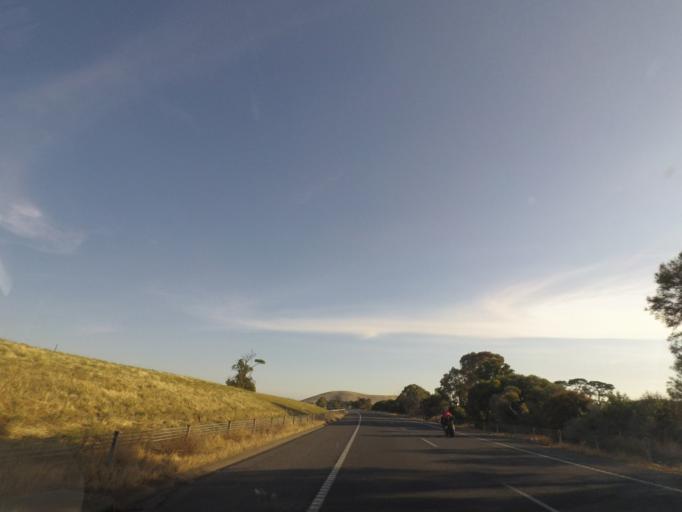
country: AU
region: Victoria
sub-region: Whittlesea
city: Whittlesea
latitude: -37.4373
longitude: 144.9817
